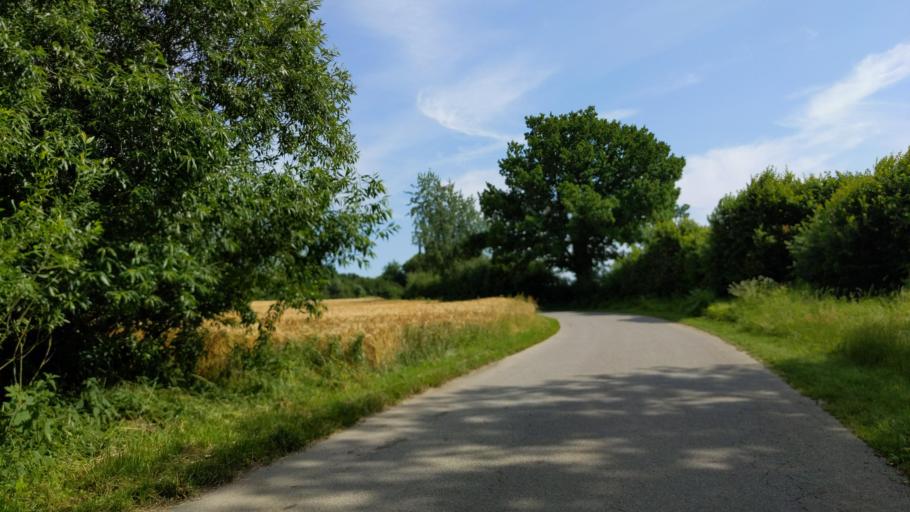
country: DE
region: Schleswig-Holstein
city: Eutin
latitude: 54.1096
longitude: 10.5947
